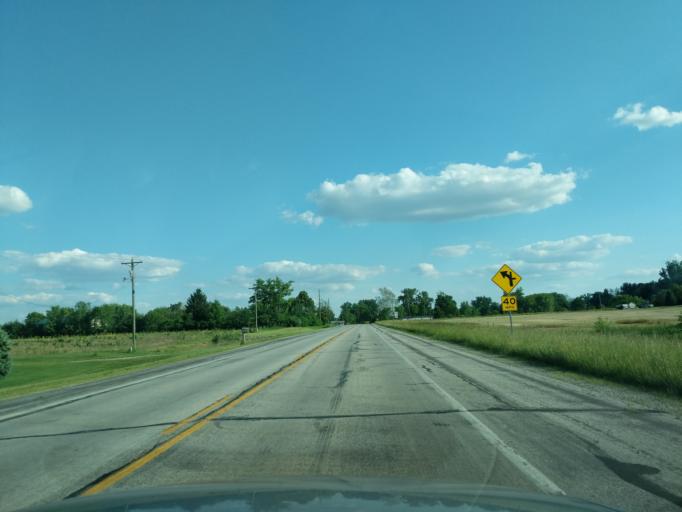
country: US
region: Indiana
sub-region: Whitley County
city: Tri-Lakes
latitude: 41.2868
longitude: -85.5007
